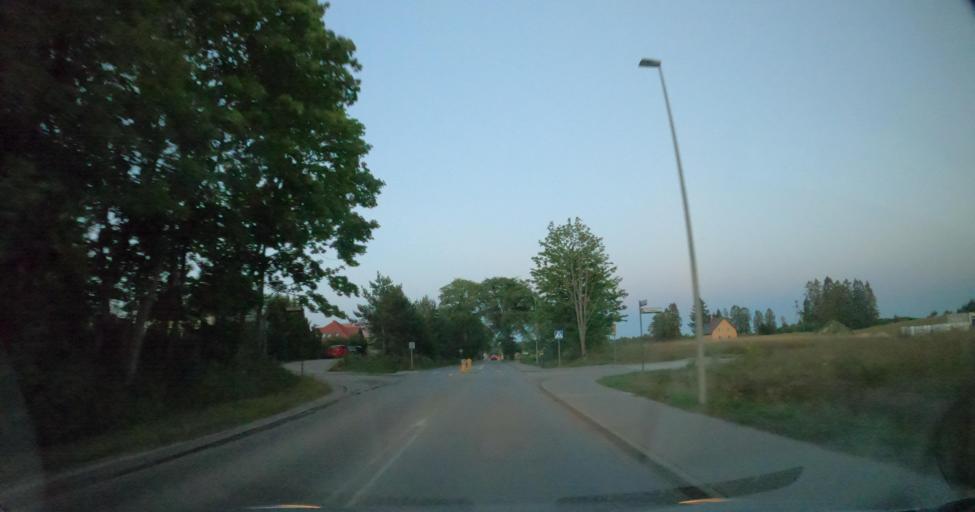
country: PL
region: Pomeranian Voivodeship
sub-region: Powiat wejherowski
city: Szemud
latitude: 54.4791
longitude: 18.2624
